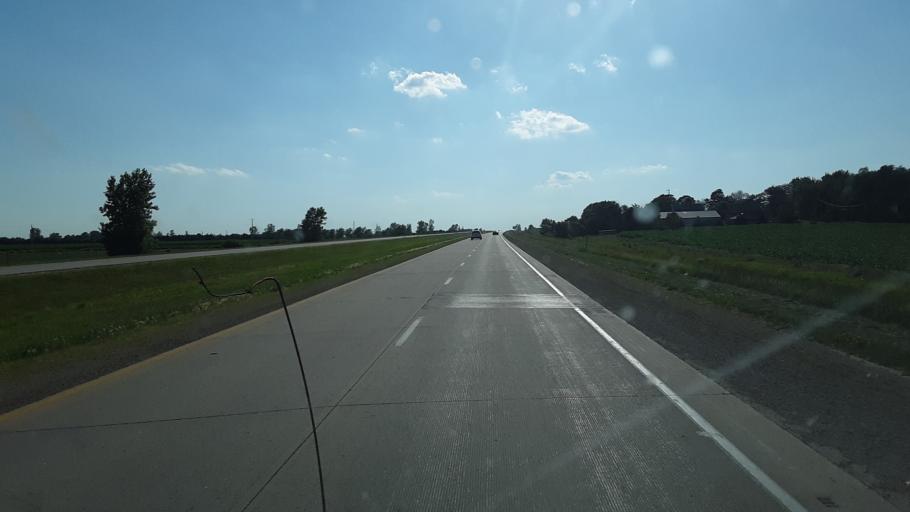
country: US
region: Iowa
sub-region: Grundy County
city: Dike
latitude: 42.4632
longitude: -92.7268
